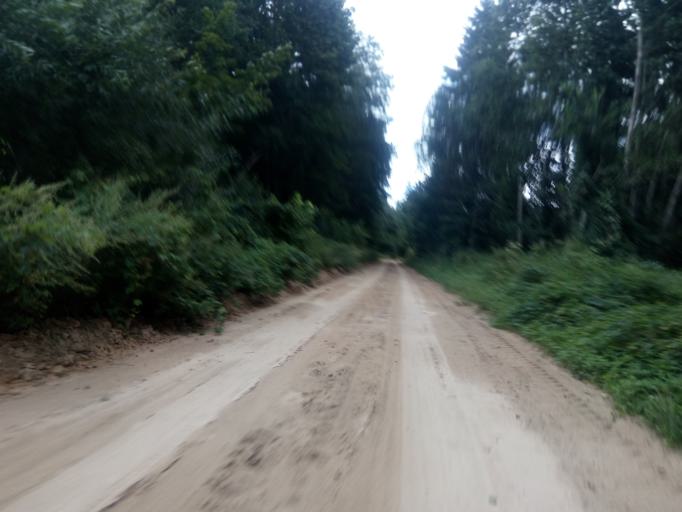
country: BY
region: Vitebsk
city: Dzisna
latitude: 55.7057
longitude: 28.3310
